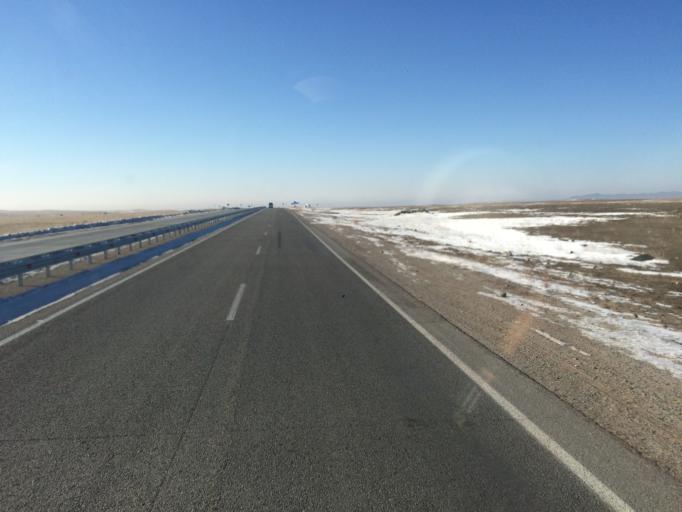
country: KZ
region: Zhambyl
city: Georgiyevka
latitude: 43.3593
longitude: 74.6219
